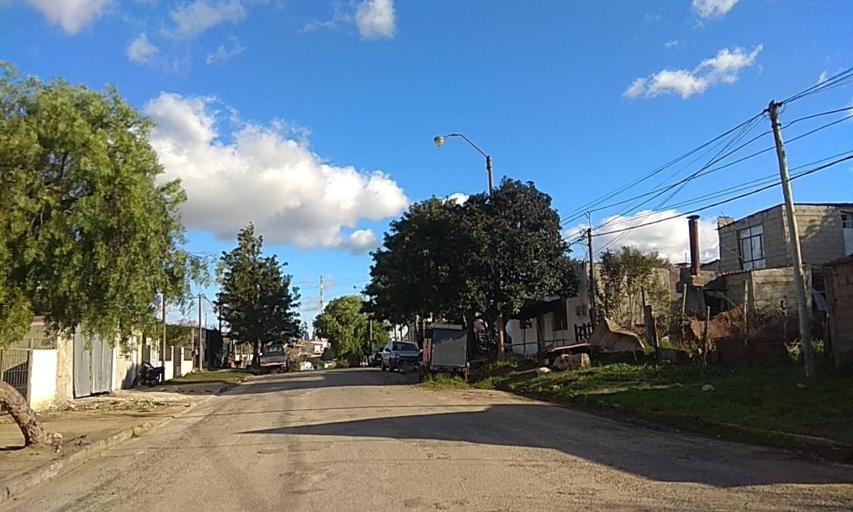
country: UY
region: Florida
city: Florida
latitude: -34.0901
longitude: -56.2103
